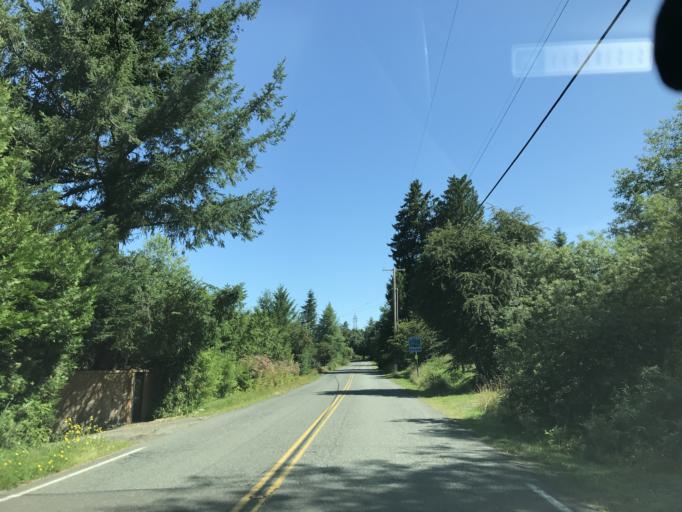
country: US
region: Washington
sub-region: King County
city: Ravensdale
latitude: 47.3581
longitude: -121.8831
